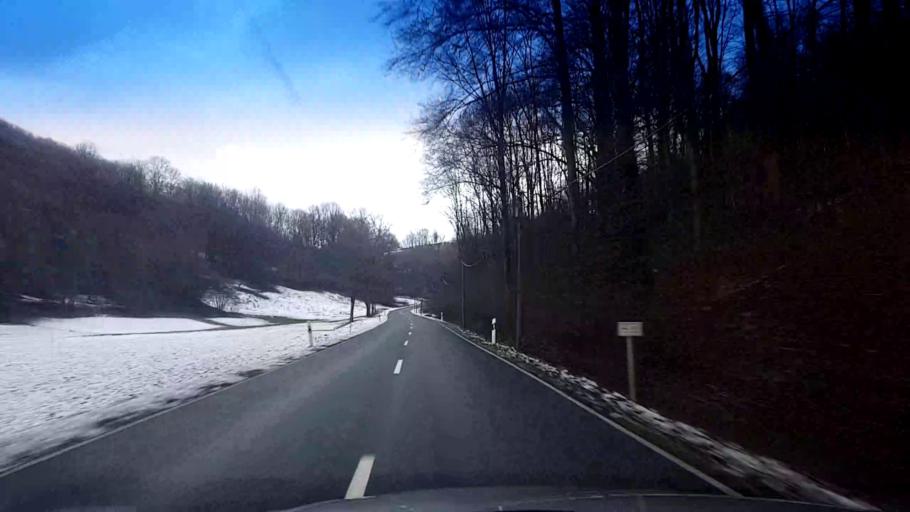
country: DE
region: Bavaria
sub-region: Upper Franconia
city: Buttenheim
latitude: 49.8445
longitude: 11.0770
